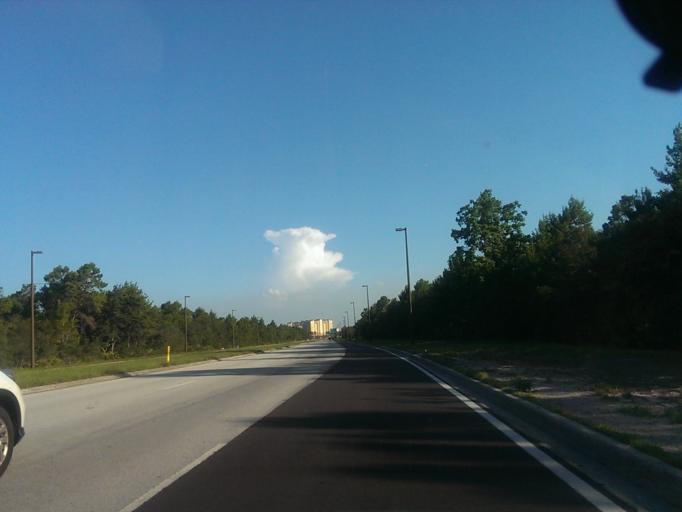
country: US
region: Florida
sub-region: Osceola County
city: Celebration
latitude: 28.3684
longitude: -81.4872
